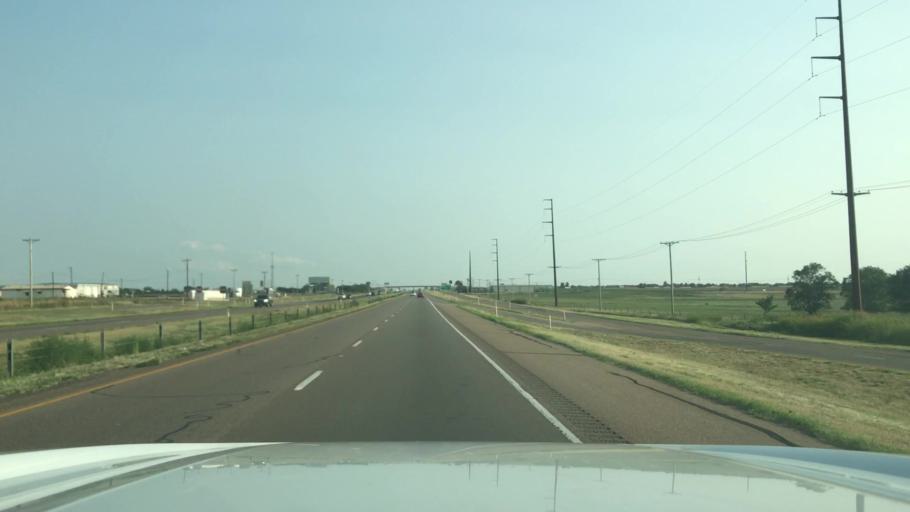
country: US
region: Texas
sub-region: Randall County
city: Canyon
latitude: 35.0559
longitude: -101.9197
